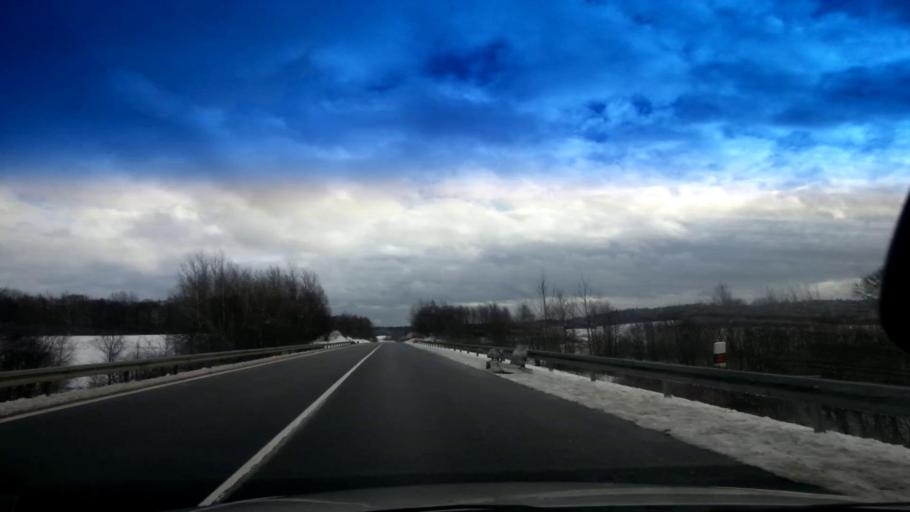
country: CZ
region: Karlovarsky
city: As
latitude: 50.2051
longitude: 12.1935
